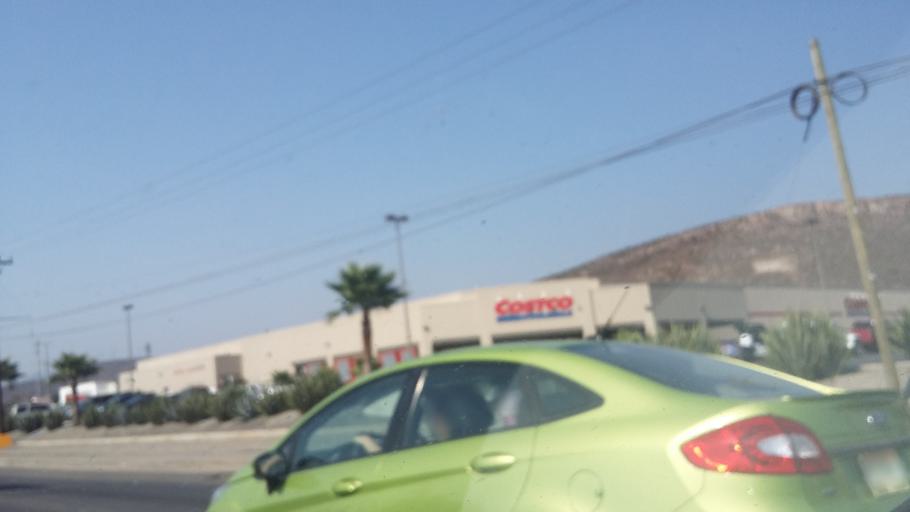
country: MX
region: Baja California
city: Ensenada
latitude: 31.8169
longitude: -116.5979
